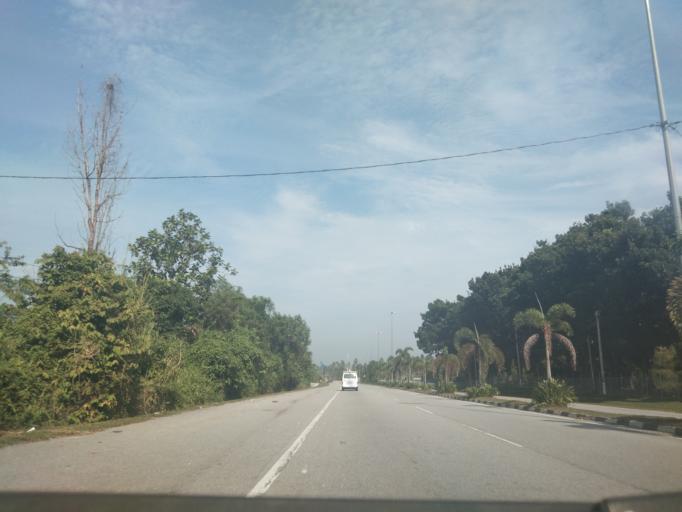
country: MY
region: Perak
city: Ipoh
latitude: 4.5007
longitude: 101.1383
